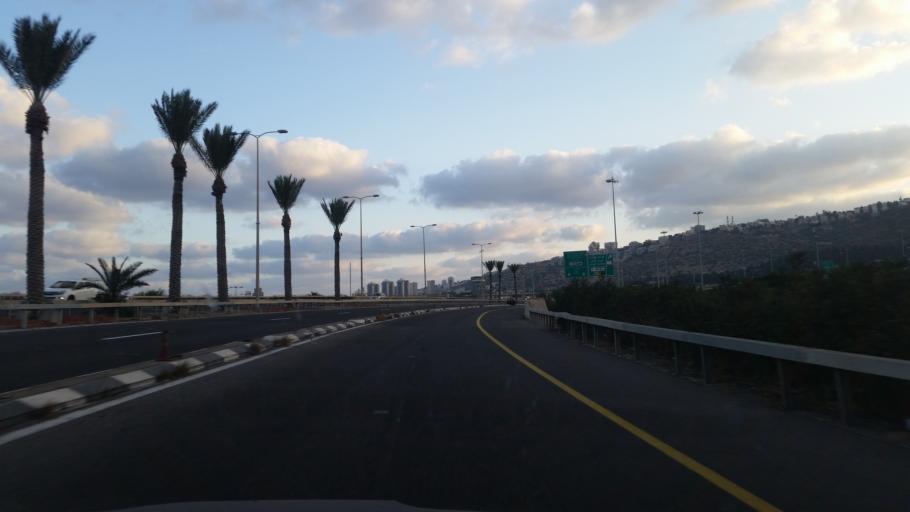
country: IL
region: Haifa
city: Tirat Karmel
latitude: 32.7899
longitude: 34.9569
